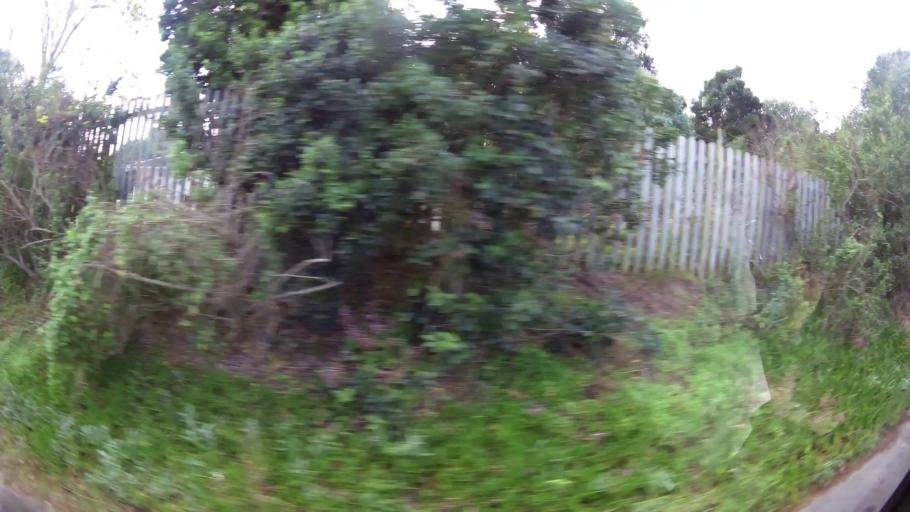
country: ZA
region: Western Cape
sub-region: Eden District Municipality
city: Knysna
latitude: -34.0559
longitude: 23.0791
